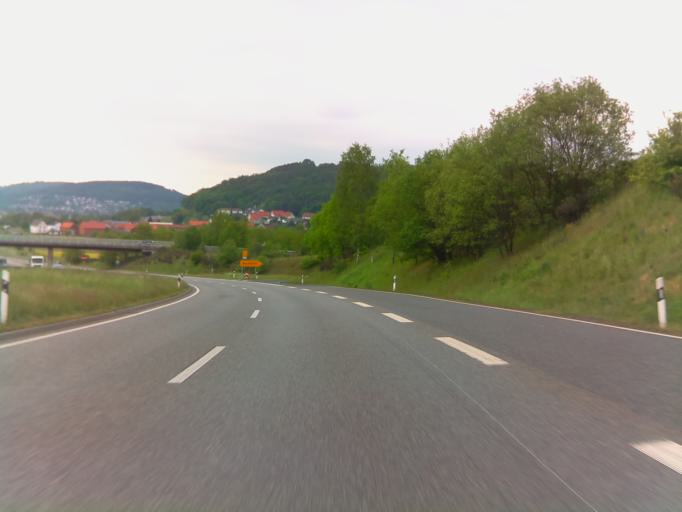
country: DE
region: Hesse
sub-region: Regierungsbezirk Giessen
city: Fronhausen
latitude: 50.7228
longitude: 8.7364
